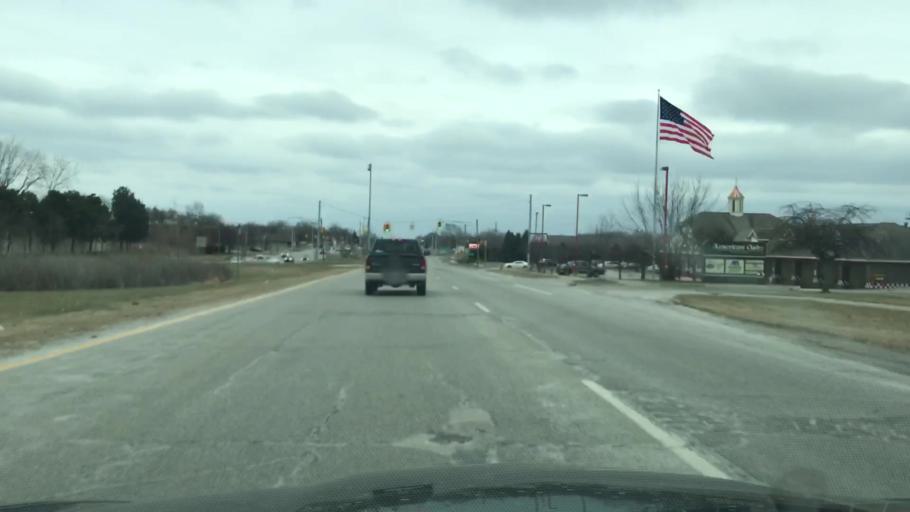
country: US
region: Michigan
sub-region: Macomb County
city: Utica
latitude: 42.6297
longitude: -83.0525
